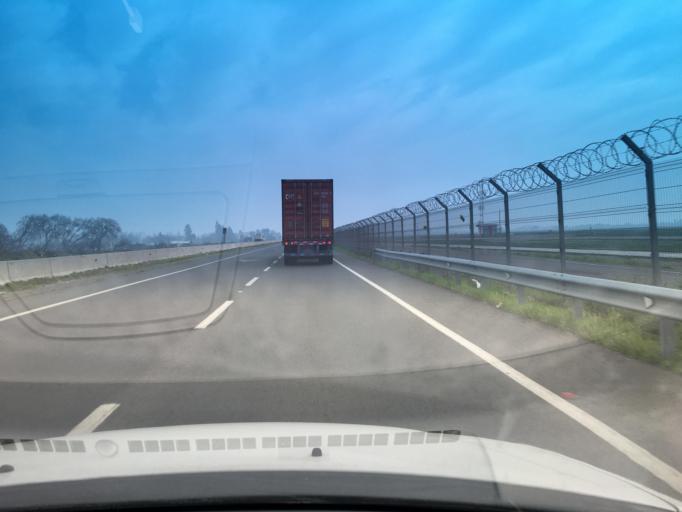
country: CL
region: Santiago Metropolitan
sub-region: Provincia de Santiago
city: Lo Prado
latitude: -33.3761
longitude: -70.8052
